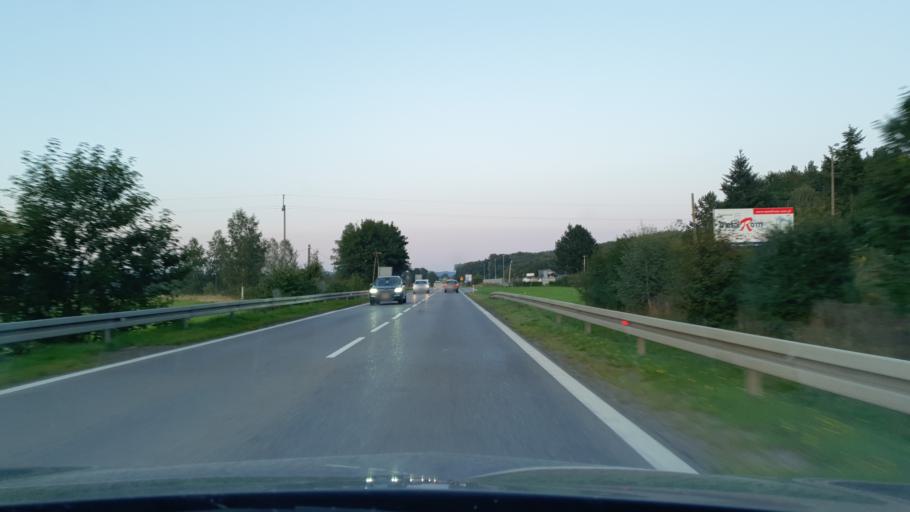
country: PL
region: Pomeranian Voivodeship
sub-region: Powiat wejherowski
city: Leczyce
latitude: 54.5643
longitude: 17.8370
